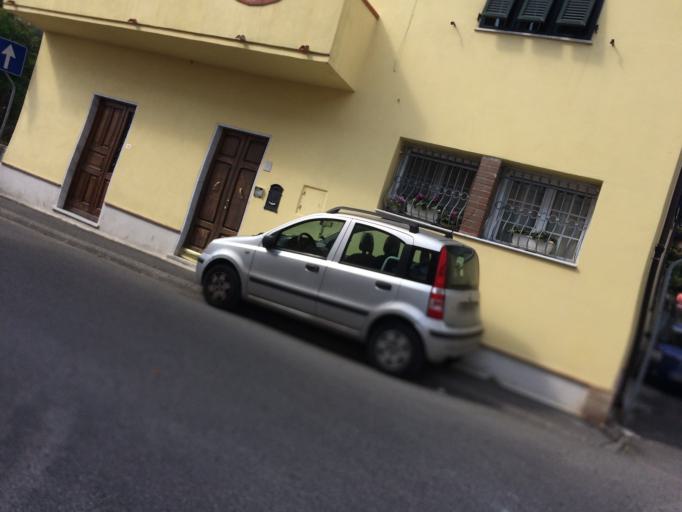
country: IT
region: Tuscany
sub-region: Provincia di Massa-Carrara
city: Carrara
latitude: 44.0725
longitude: 10.0784
